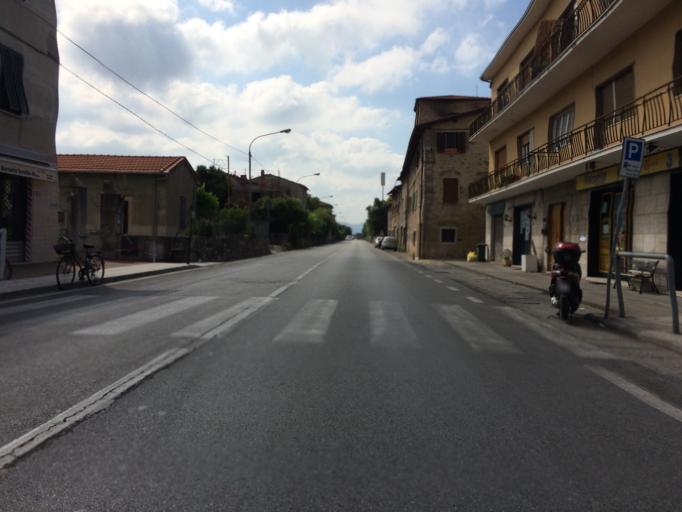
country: IT
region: Tuscany
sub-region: Provincia di Lucca
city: Ripa-Pozzi-Querceta-Ponterosso
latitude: 43.9759
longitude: 10.2014
